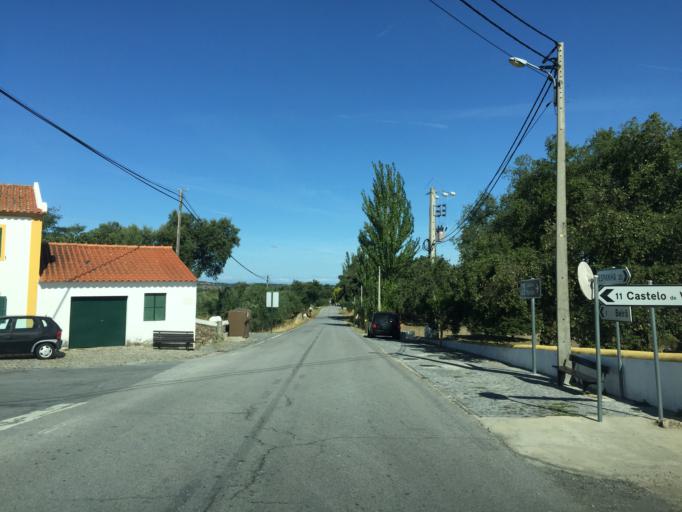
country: PT
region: Portalegre
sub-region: Marvao
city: Marvao
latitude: 39.4348
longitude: -7.3636
